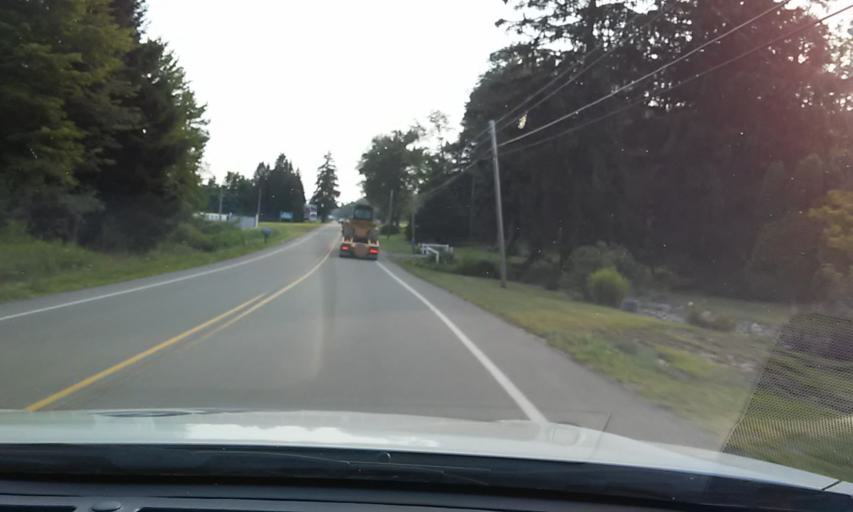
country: US
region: Pennsylvania
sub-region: McKean County
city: Kane
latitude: 41.7212
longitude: -78.6833
